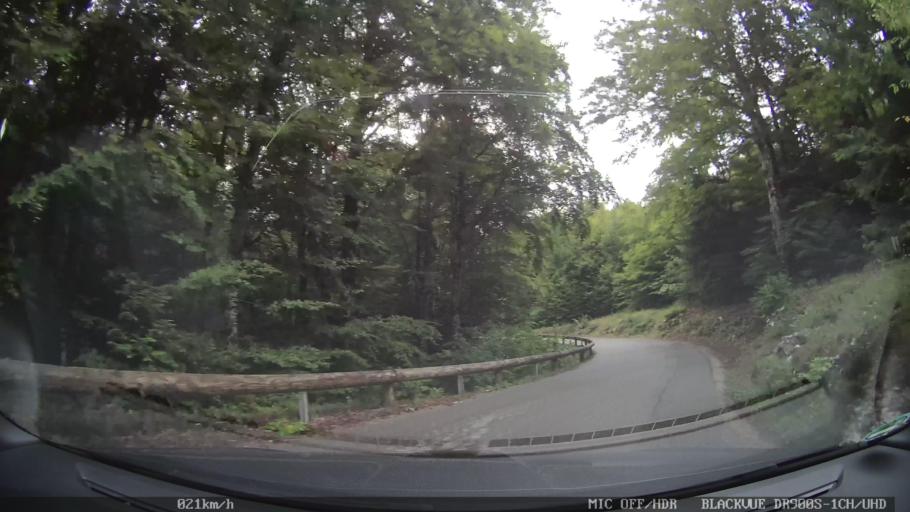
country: HR
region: Licko-Senjska
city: Jezerce
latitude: 44.9270
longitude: 15.5813
